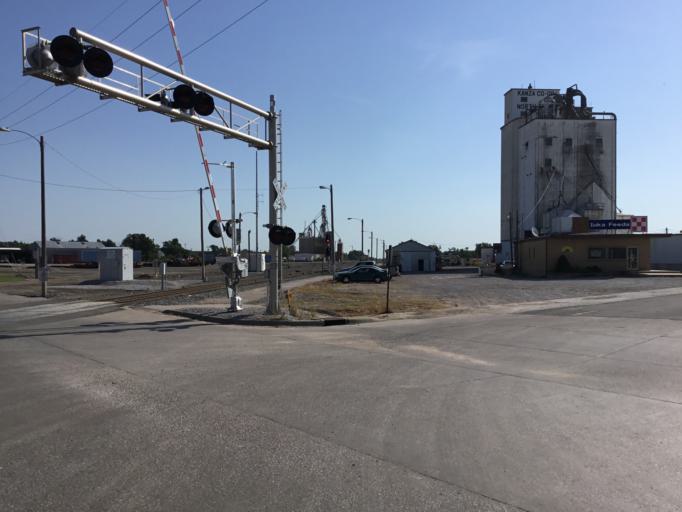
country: US
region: Kansas
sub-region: Pratt County
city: Pratt
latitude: 37.6531
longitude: -98.7394
